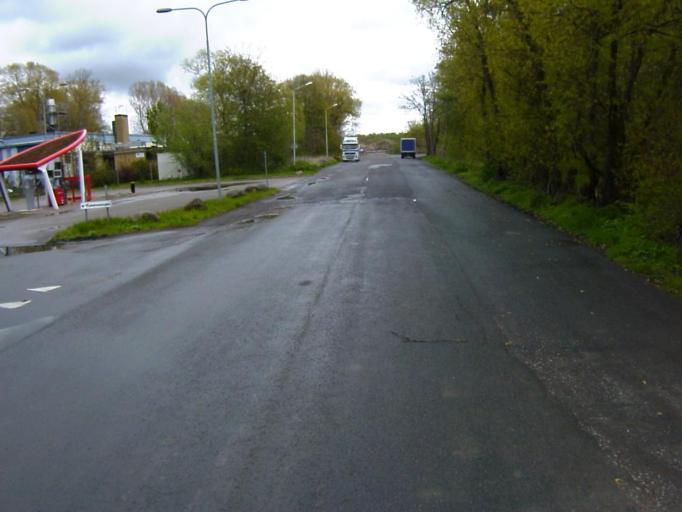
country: SE
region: Skane
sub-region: Kristianstads Kommun
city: Kristianstad
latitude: 56.0235
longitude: 14.1739
